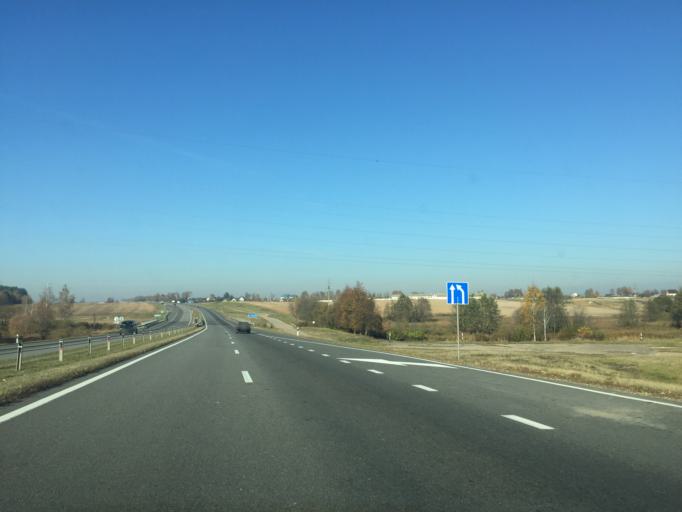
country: BY
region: Mogilev
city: Buynichy
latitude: 53.9579
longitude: 30.2028
